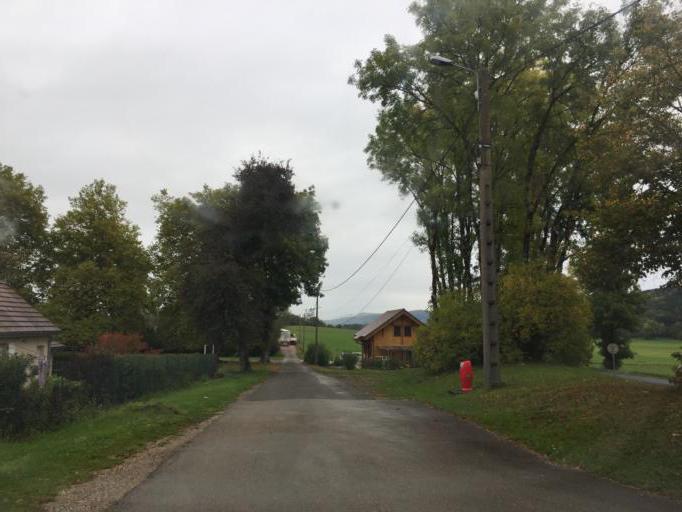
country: FR
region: Franche-Comte
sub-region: Departement du Jura
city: Orgelet
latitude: 46.5100
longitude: 5.5688
